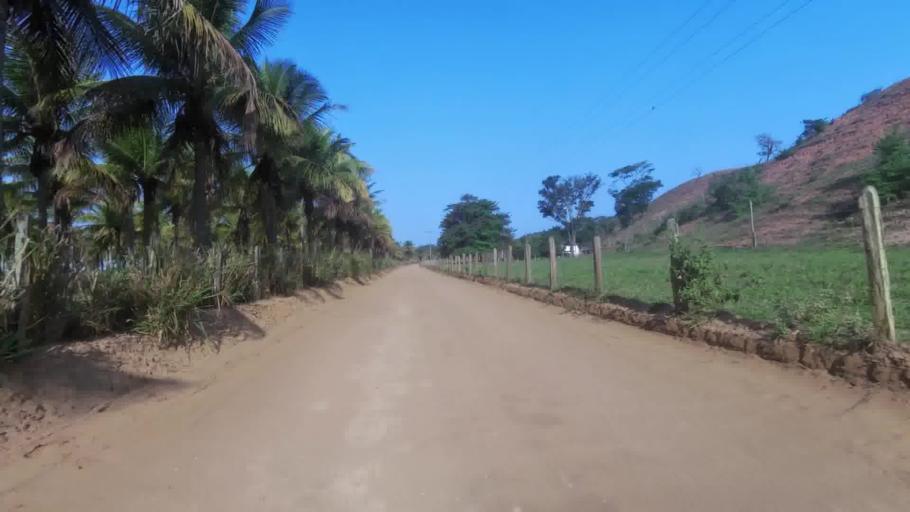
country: BR
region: Espirito Santo
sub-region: Piuma
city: Piuma
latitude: -20.8476
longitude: -40.7674
